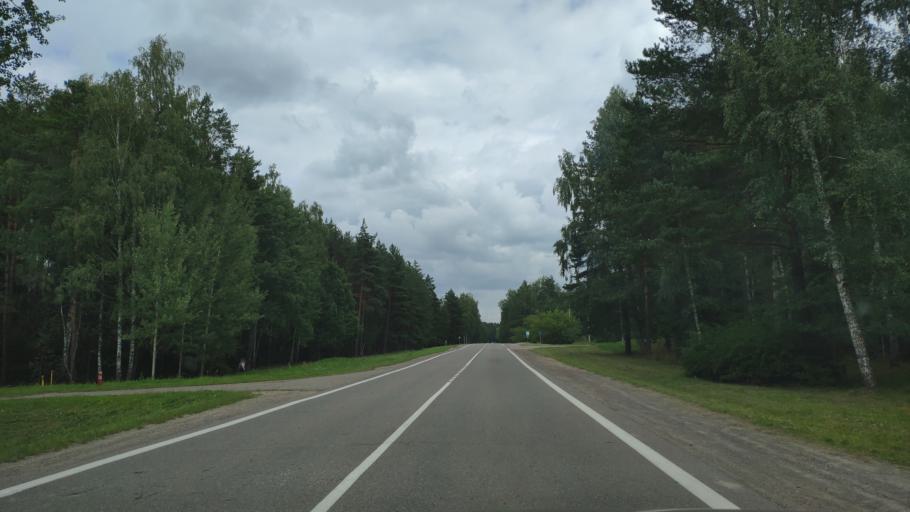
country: BY
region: Minsk
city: Zhdanovichy
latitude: 53.9717
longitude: 27.4344
